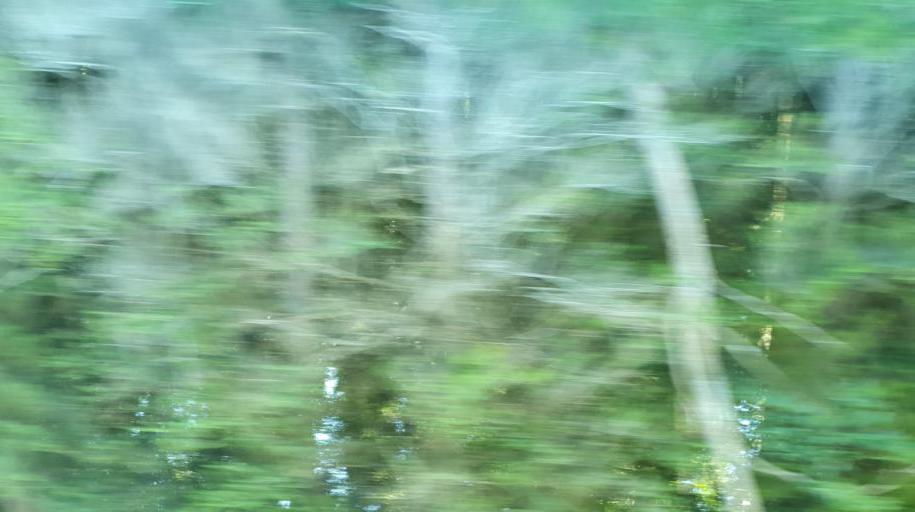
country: NO
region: Nord-Trondelag
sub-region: Levanger
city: Levanger
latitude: 63.6966
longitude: 11.2694
